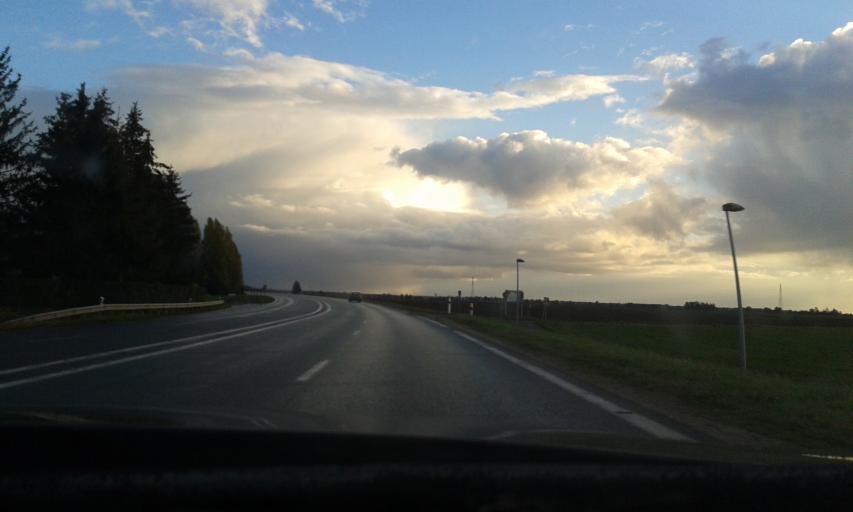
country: FR
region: Centre
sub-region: Departement du Loiret
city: Artenay
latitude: 48.0786
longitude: 1.8733
